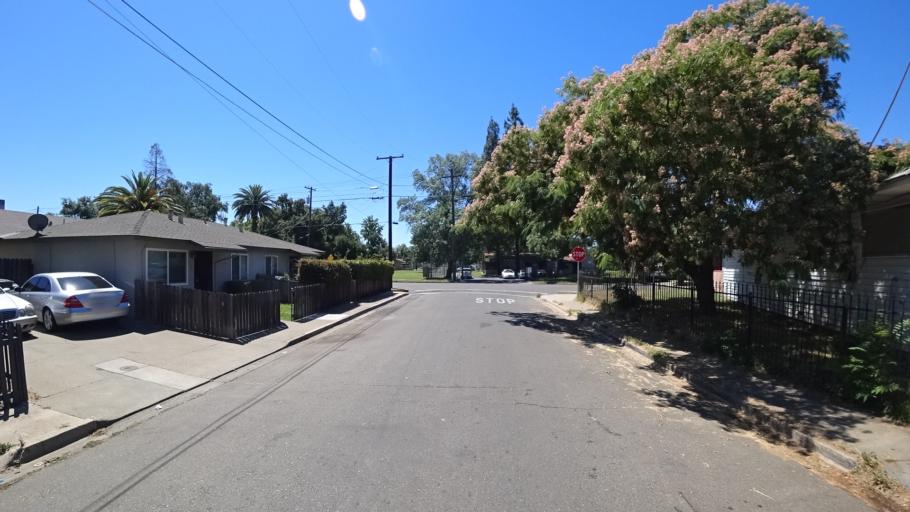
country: US
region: California
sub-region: Sacramento County
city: Sacramento
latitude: 38.5486
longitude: -121.4602
